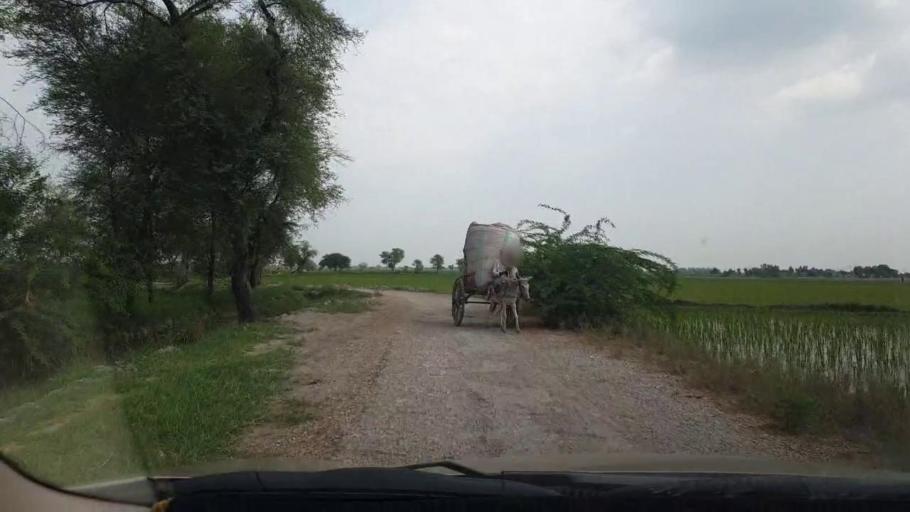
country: PK
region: Sindh
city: Larkana
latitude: 27.5133
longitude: 68.1312
